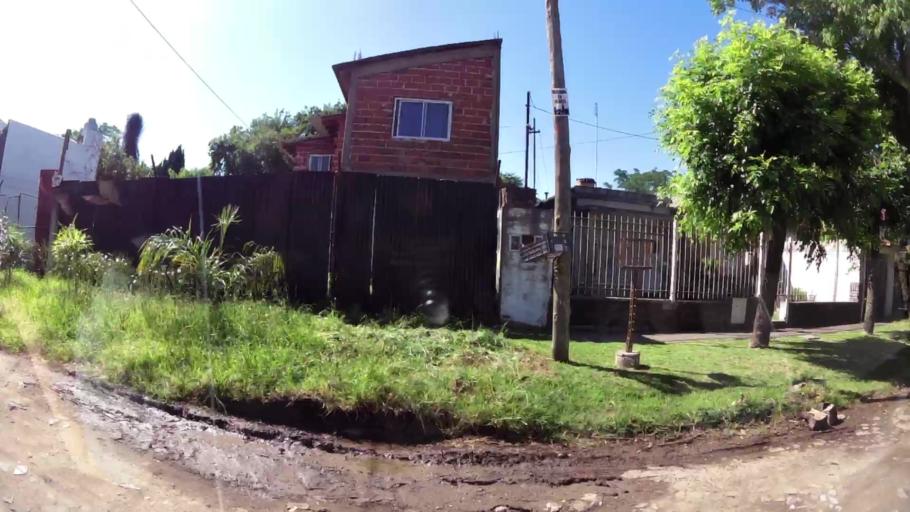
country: AR
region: Buenos Aires
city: Ituzaingo
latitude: -34.6292
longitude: -58.6561
